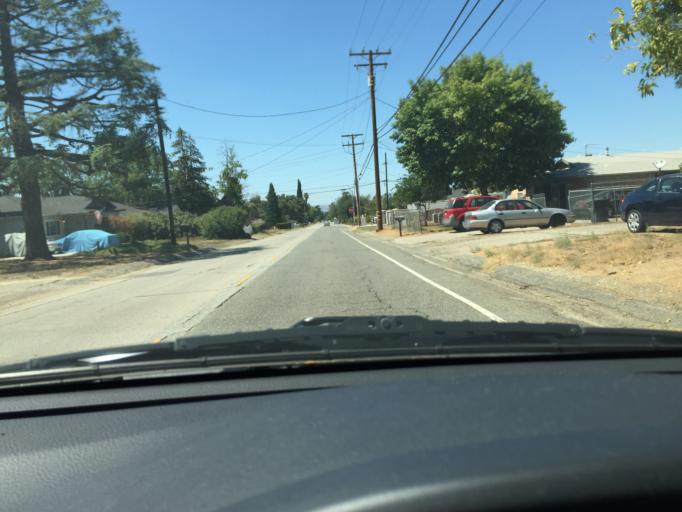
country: US
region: California
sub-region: San Bernardino County
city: Yucaipa
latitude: 34.0047
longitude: -117.0245
